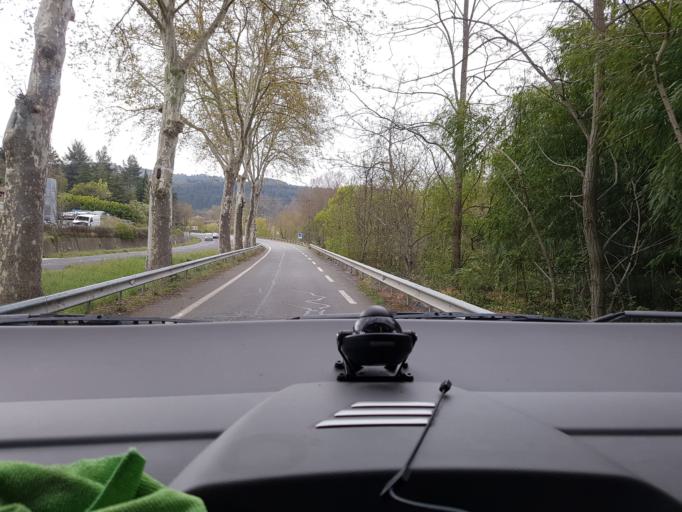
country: FR
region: Languedoc-Roussillon
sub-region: Departement de l'Aude
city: Couiza
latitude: 42.9491
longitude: 2.2534
